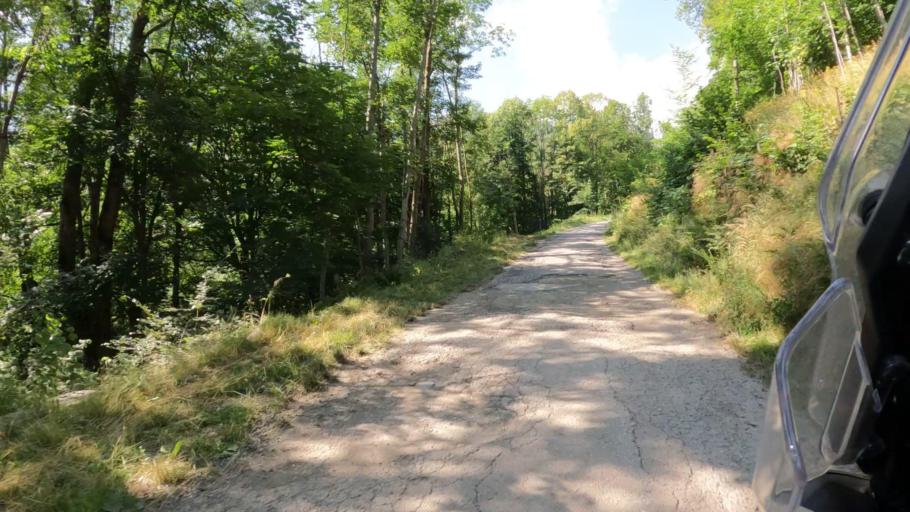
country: IT
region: Piedmont
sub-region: Provincia di Torino
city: Lemie
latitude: 45.2102
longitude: 7.3098
